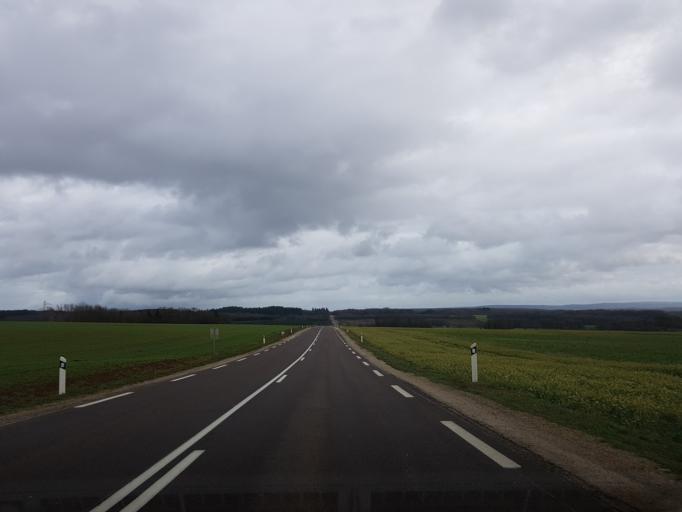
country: FR
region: Franche-Comte
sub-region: Departement de la Haute-Saone
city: Scey-sur-Saone-et-Saint-Albin
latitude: 47.7045
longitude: 5.9354
